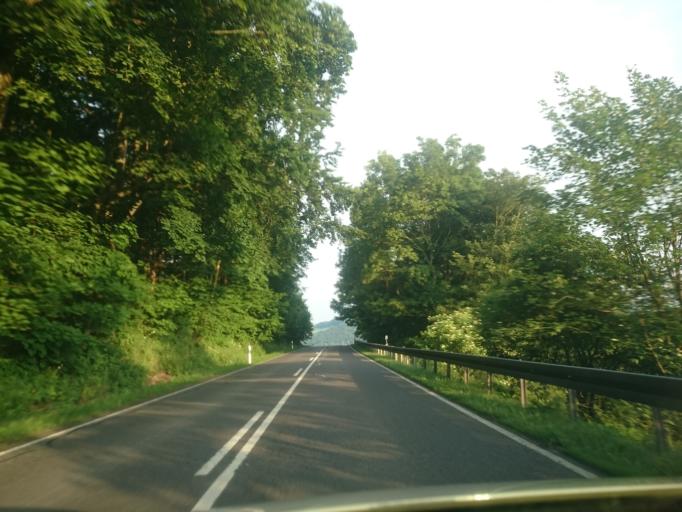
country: DE
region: Saxony
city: Pockau
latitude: 50.7104
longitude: 13.2369
